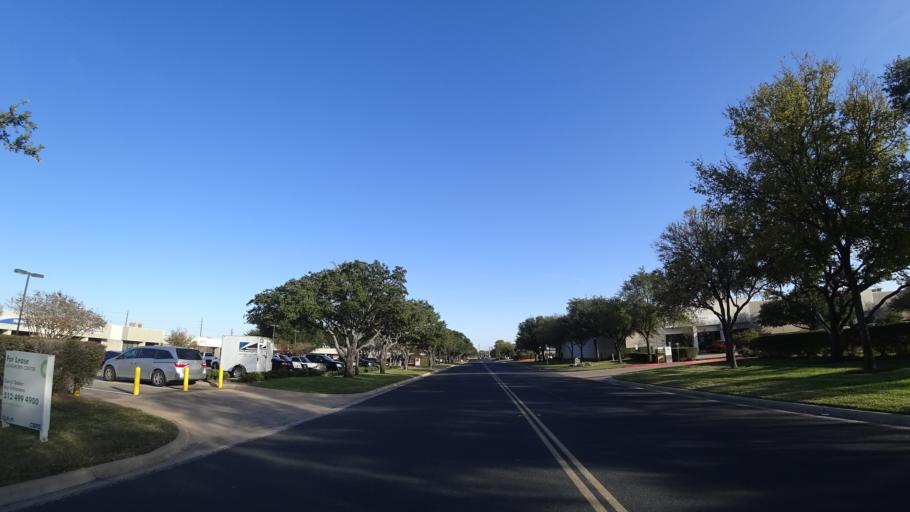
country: US
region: Texas
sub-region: Williamson County
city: Jollyville
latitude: 30.3817
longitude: -97.7284
